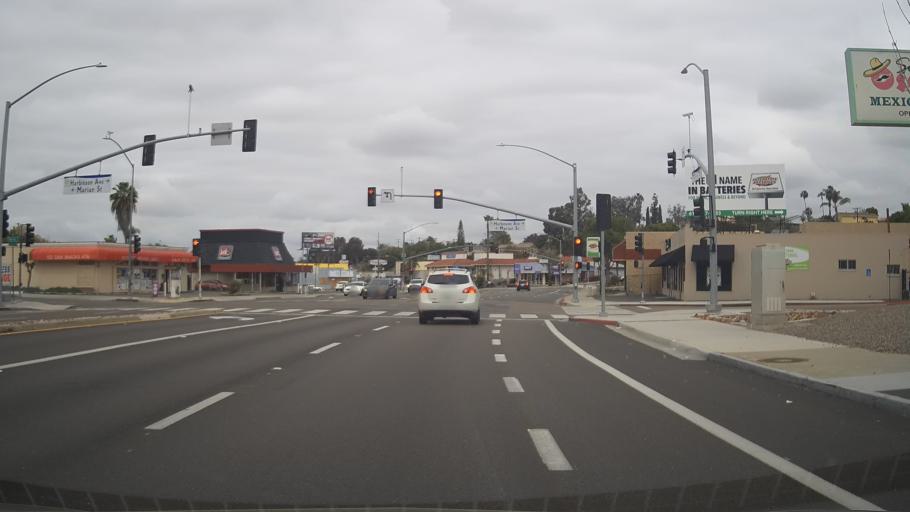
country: US
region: California
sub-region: San Diego County
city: Lemon Grove
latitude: 32.7553
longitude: -117.0465
